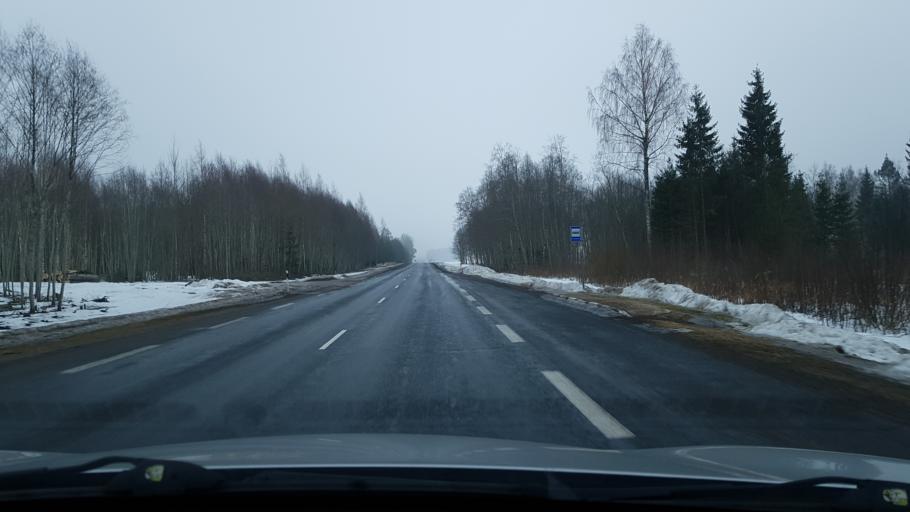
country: EE
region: Valgamaa
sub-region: Torva linn
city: Torva
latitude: 58.1172
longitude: 25.9963
